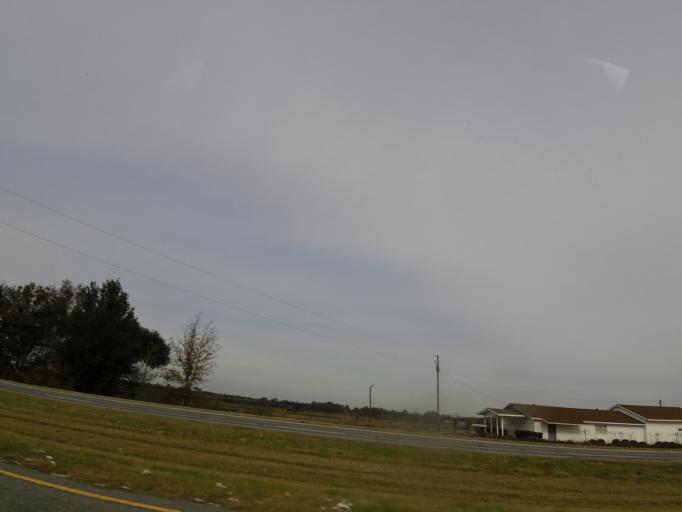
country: US
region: Georgia
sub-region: Seminole County
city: Donalsonville
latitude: 31.0165
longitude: -84.8210
